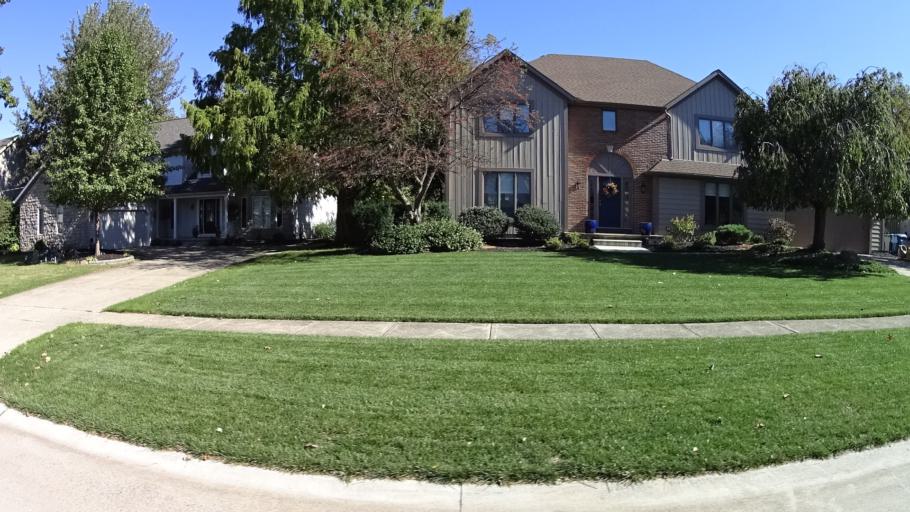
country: US
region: Ohio
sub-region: Lorain County
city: Amherst
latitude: 41.3829
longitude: -82.2267
